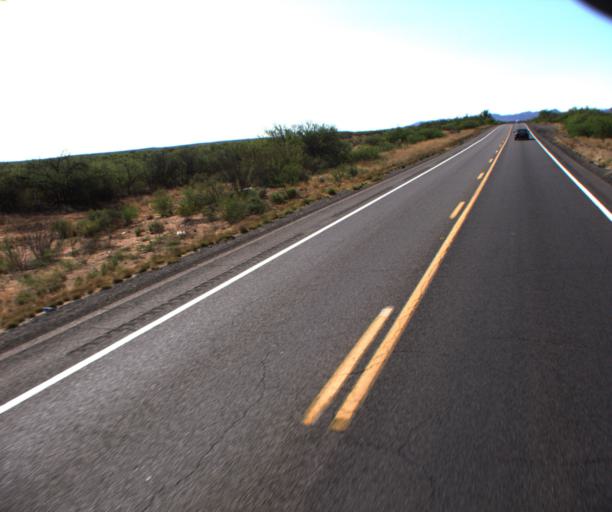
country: US
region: Arizona
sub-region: Cochise County
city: Saint David
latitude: 31.8023
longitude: -110.1590
